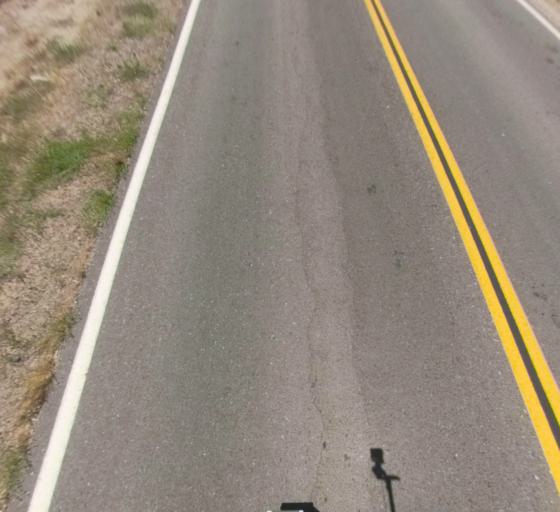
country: US
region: California
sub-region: Madera County
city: Bonadelle Ranchos-Madera Ranchos
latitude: 36.9941
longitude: -119.8937
